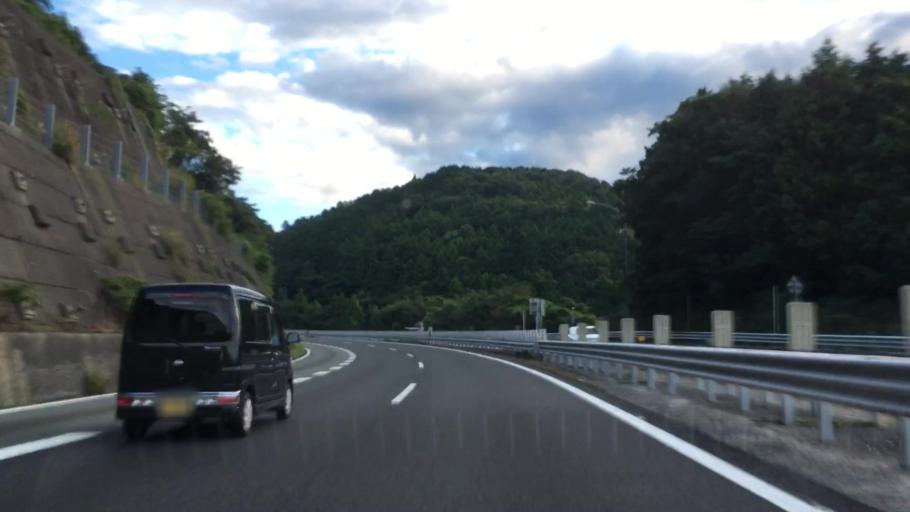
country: JP
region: Yamaguchi
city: Onoda
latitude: 34.1515
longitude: 131.2345
